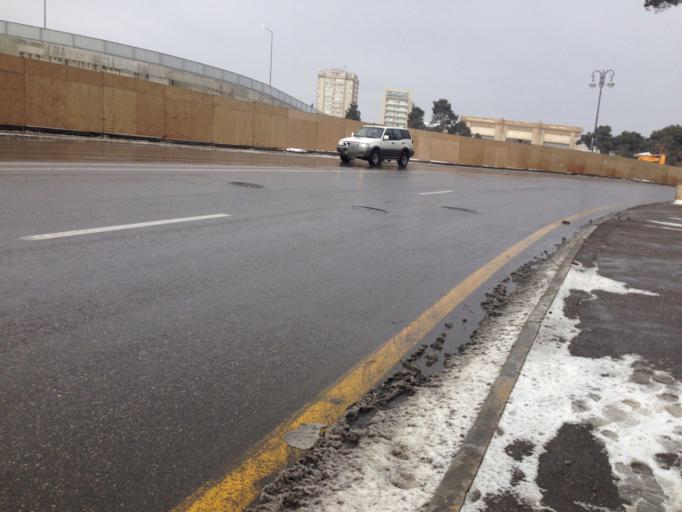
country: AZ
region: Baki
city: Baku
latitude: 40.3972
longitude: 49.8504
